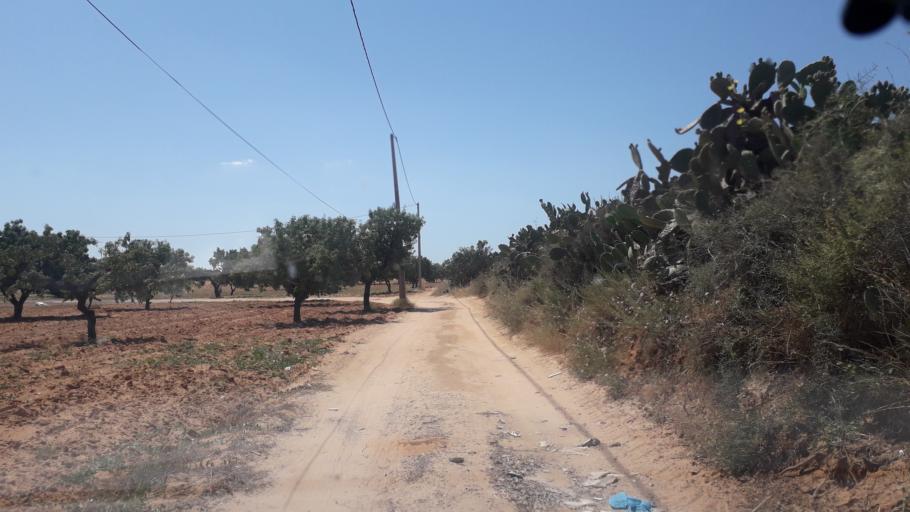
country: TN
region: Safaqis
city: Al Qarmadah
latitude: 34.8301
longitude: 10.7689
